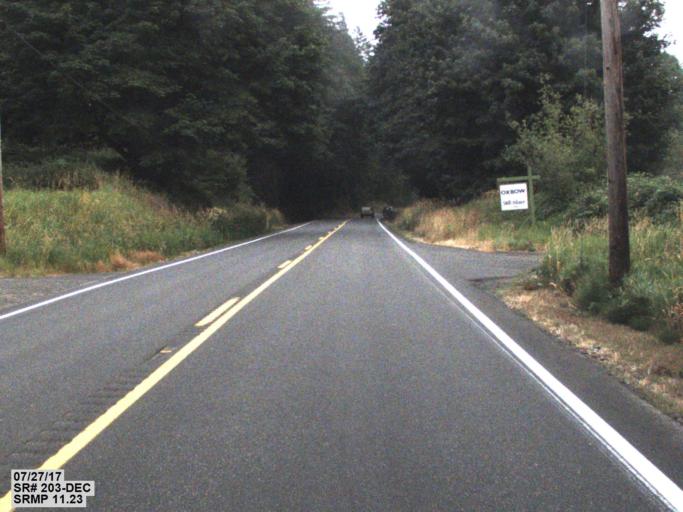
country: US
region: Washington
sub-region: King County
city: Duvall
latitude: 47.6936
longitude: -121.9681
